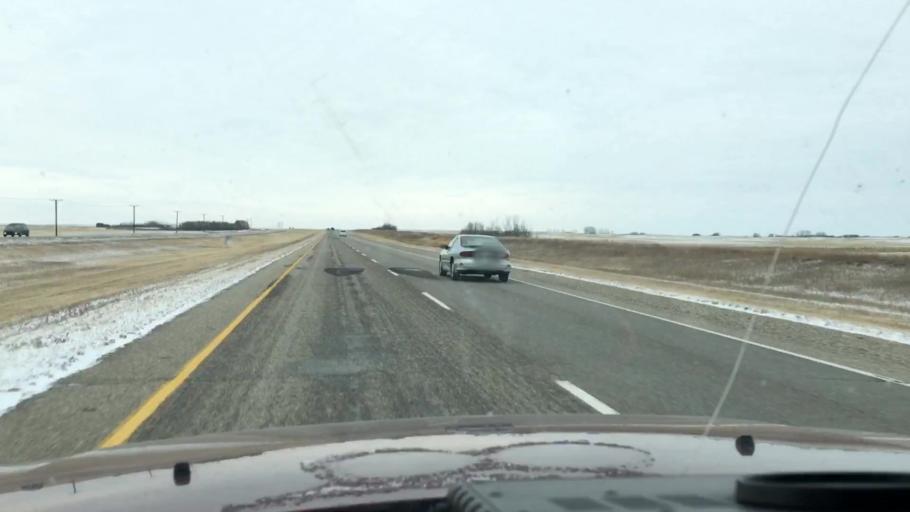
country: CA
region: Saskatchewan
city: Watrous
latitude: 51.4262
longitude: -106.1972
